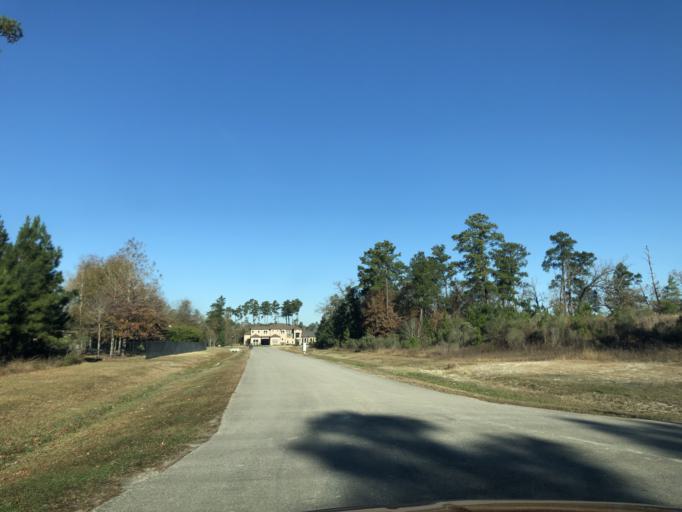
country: US
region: Texas
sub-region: Montgomery County
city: Porter Heights
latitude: 30.0695
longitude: -95.3181
